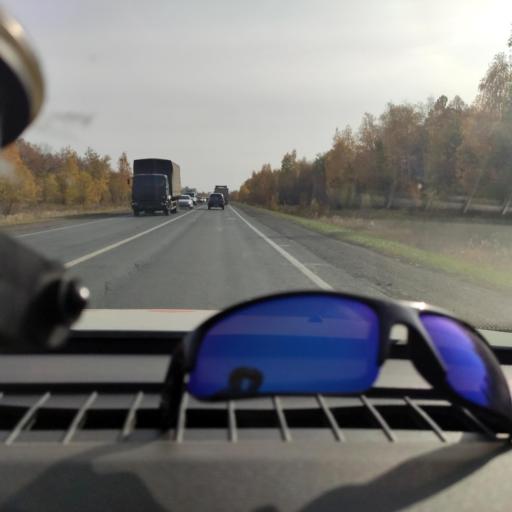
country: RU
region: Samara
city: Chapayevsk
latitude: 52.9938
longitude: 49.8209
